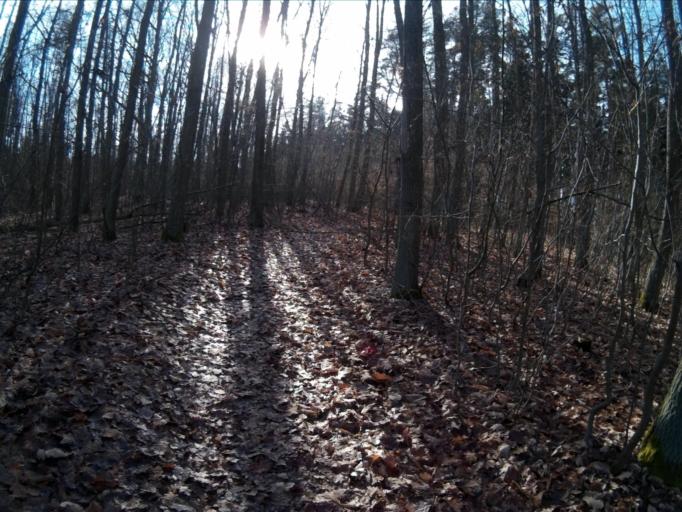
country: CZ
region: Vysocina
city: Mohelno
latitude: 49.1410
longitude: 16.2023
